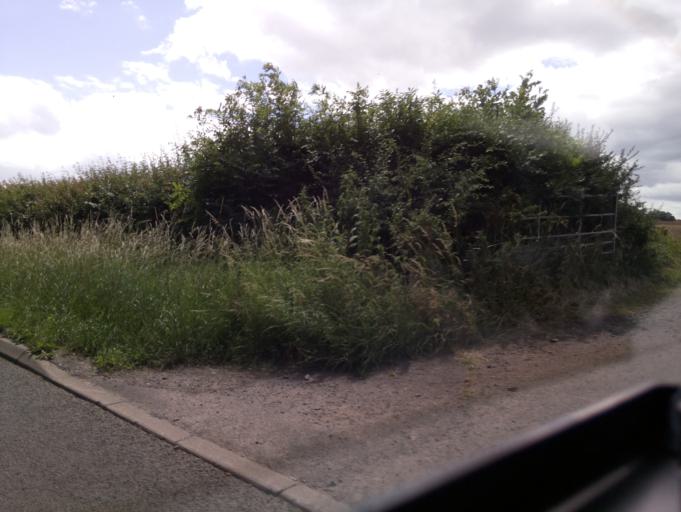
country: GB
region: England
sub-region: Nottinghamshire
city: Cotgrave
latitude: 52.8854
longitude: -1.0851
